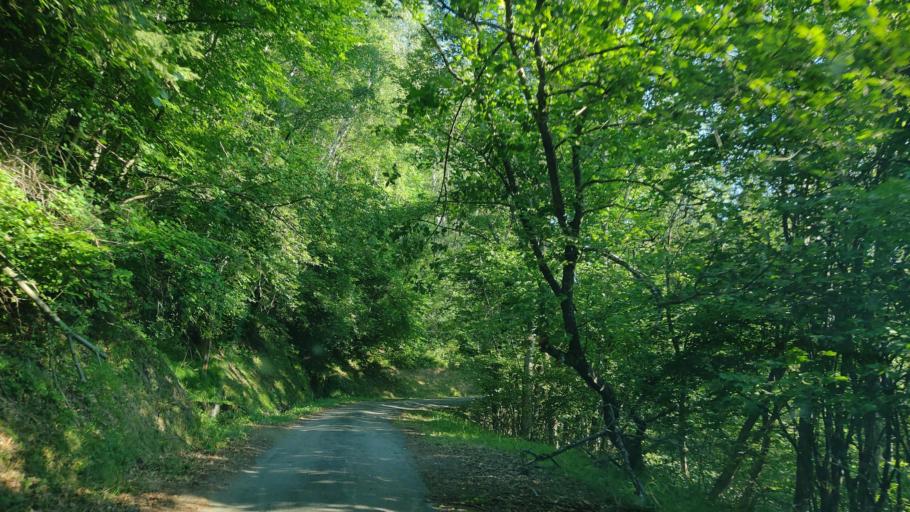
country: FR
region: Rhone-Alpes
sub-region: Departement de la Savoie
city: Saint-Etienne-de-Cuines
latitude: 45.3408
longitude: 6.2757
